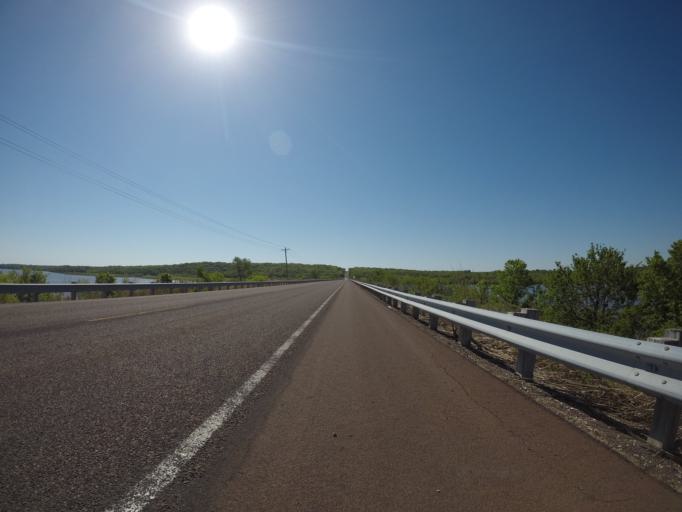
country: US
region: Kansas
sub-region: Osage County
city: Overbrook
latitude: 38.9029
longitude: -95.4440
